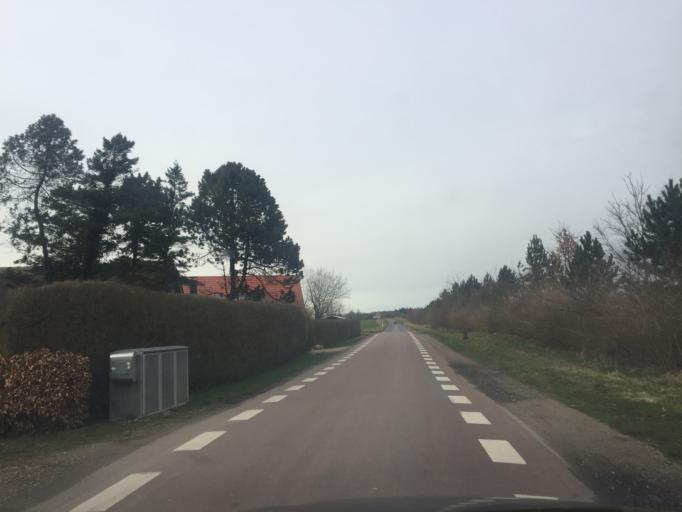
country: DK
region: Zealand
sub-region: Ringsted Kommune
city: Ringsted
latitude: 55.4931
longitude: 11.8220
